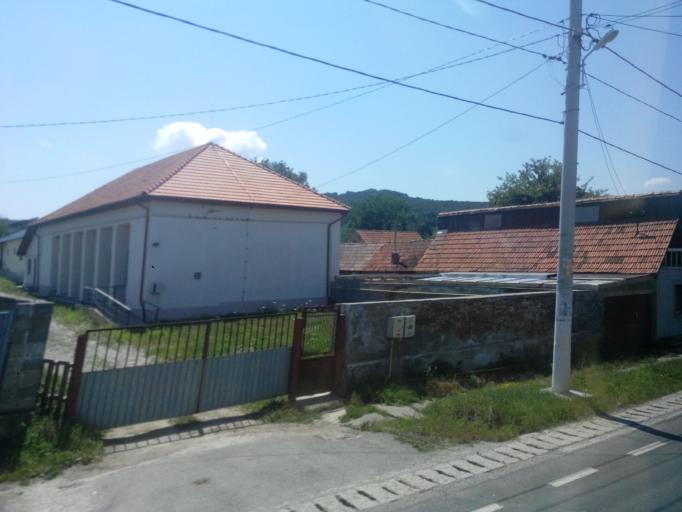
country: RO
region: Hunedoara
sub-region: Comuna Turdas
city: Turdas
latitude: 45.8342
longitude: 23.0900
